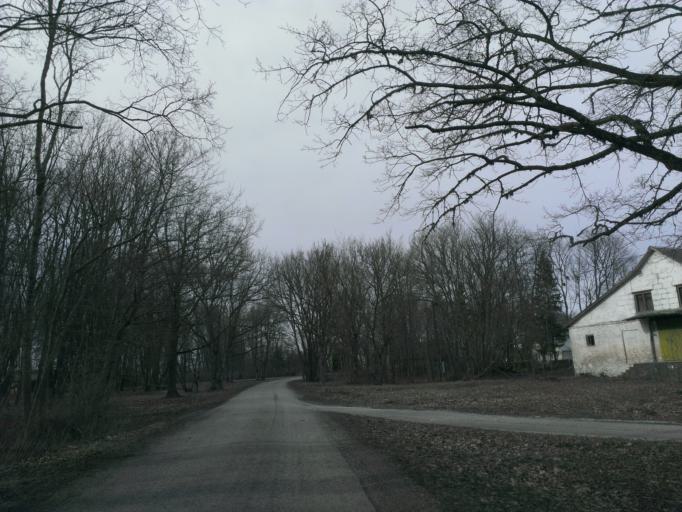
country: EE
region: Laeaene
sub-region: Lihula vald
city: Lihula
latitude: 58.5812
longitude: 23.5387
